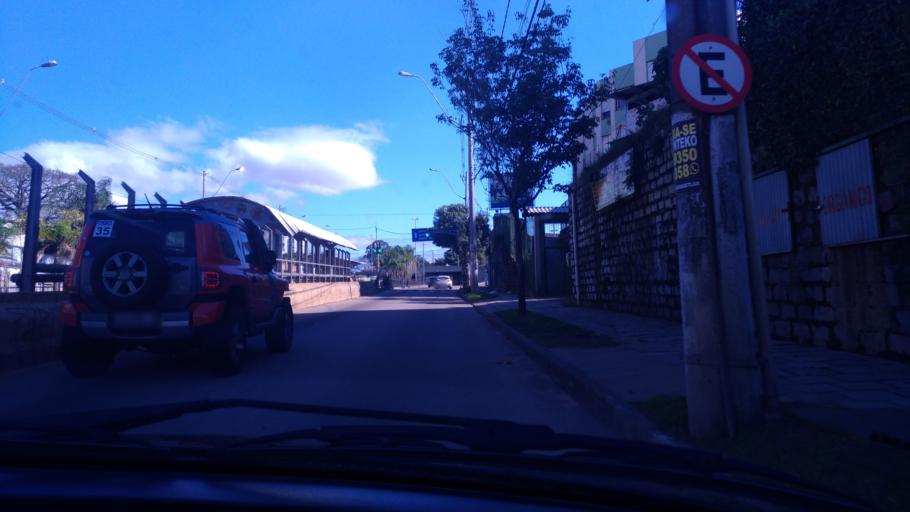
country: BR
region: Rio Grande do Sul
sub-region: Porto Alegre
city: Porto Alegre
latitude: -30.0762
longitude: -51.2062
